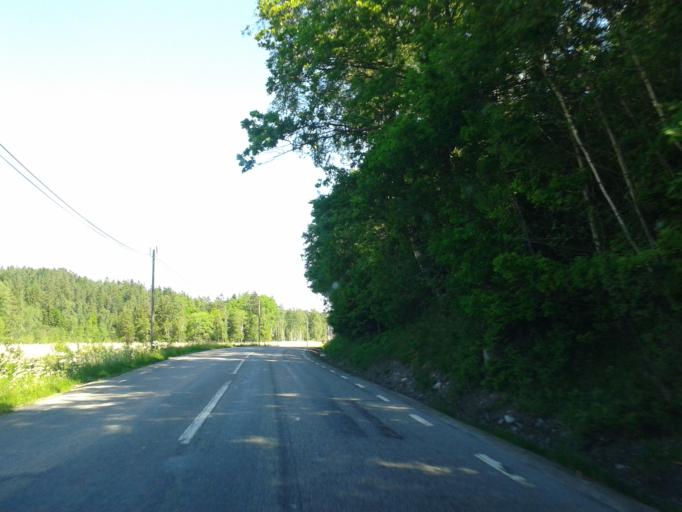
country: SE
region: Vaestra Goetaland
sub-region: Orust
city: Henan
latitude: 58.2335
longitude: 11.6944
